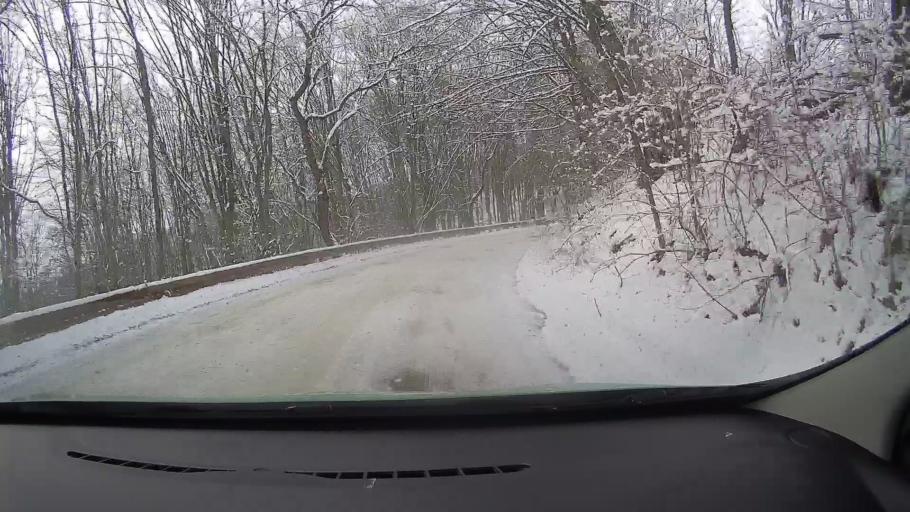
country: RO
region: Alba
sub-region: Comuna Almasu Mare
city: Almasu Mare
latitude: 46.0935
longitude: 23.1680
